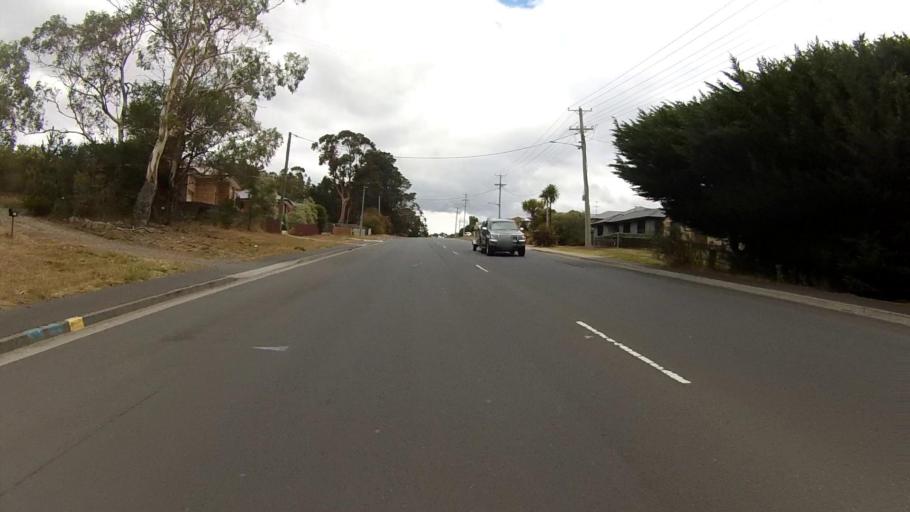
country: AU
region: Tasmania
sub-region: Glenorchy
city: Austins Ferry
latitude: -42.7688
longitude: 147.2454
